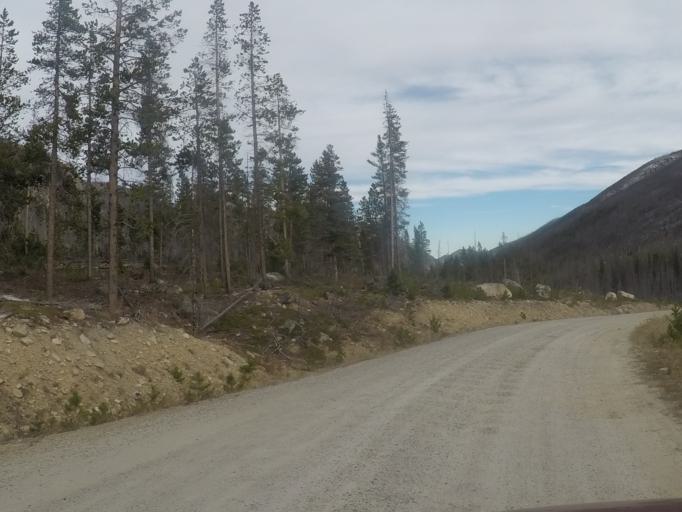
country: US
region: Montana
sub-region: Carbon County
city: Red Lodge
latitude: 45.1743
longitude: -109.4406
